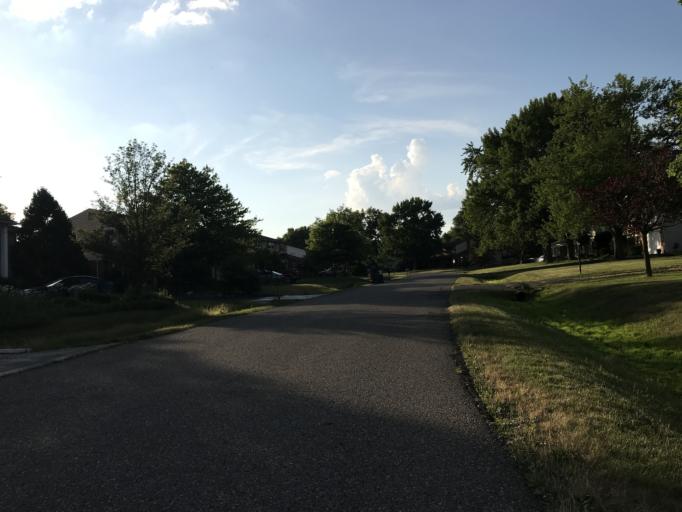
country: US
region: Michigan
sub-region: Oakland County
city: Farmington Hills
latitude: 42.4880
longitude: -83.3431
